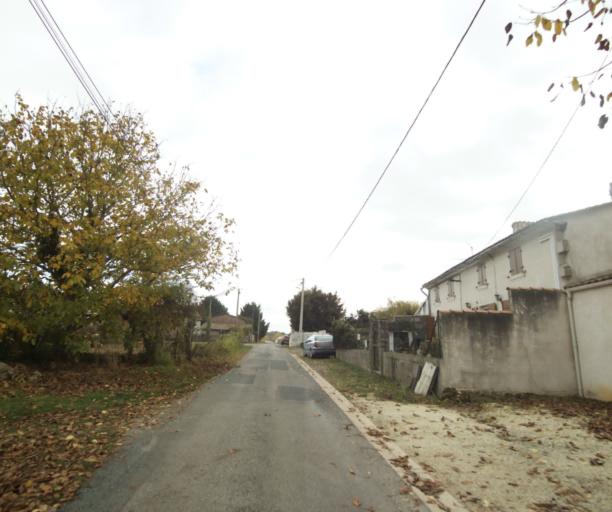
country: FR
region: Poitou-Charentes
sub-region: Departement de la Charente-Maritime
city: Saint-Georges-des-Coteaux
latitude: 45.7809
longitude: -0.7133
